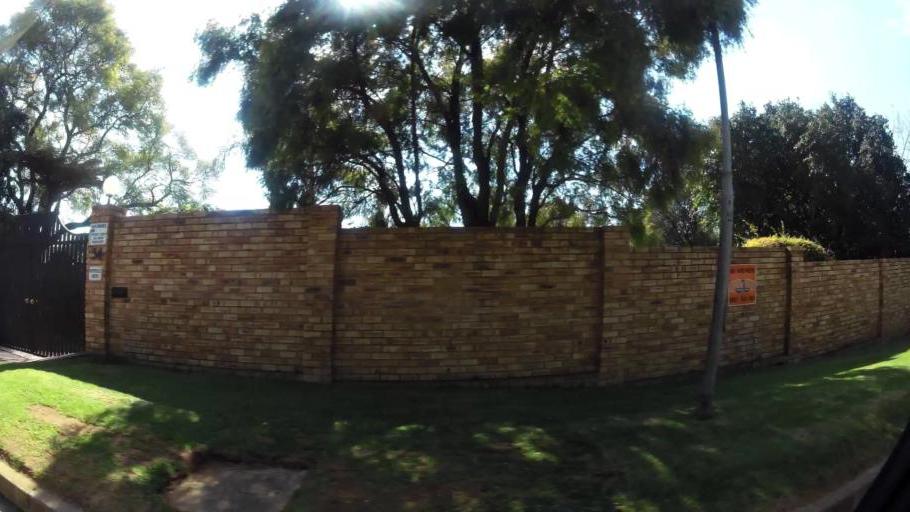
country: ZA
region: Gauteng
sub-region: City of Johannesburg Metropolitan Municipality
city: Roodepoort
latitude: -26.0773
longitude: 27.9409
